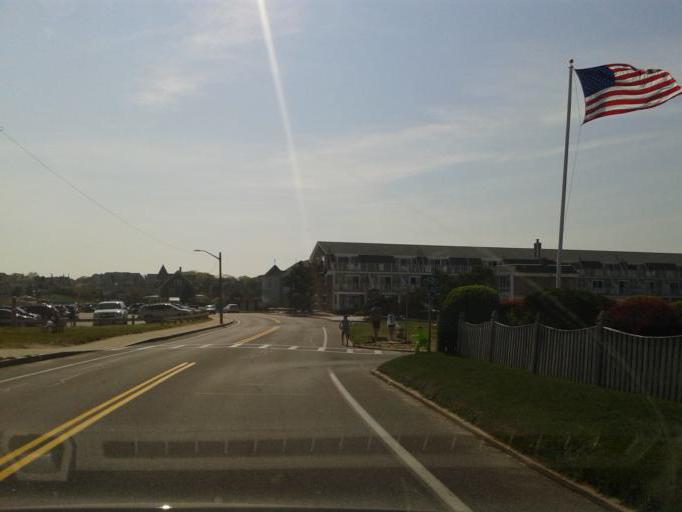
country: US
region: Massachusetts
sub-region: Barnstable County
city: Teaticket
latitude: 41.5459
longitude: -70.5936
